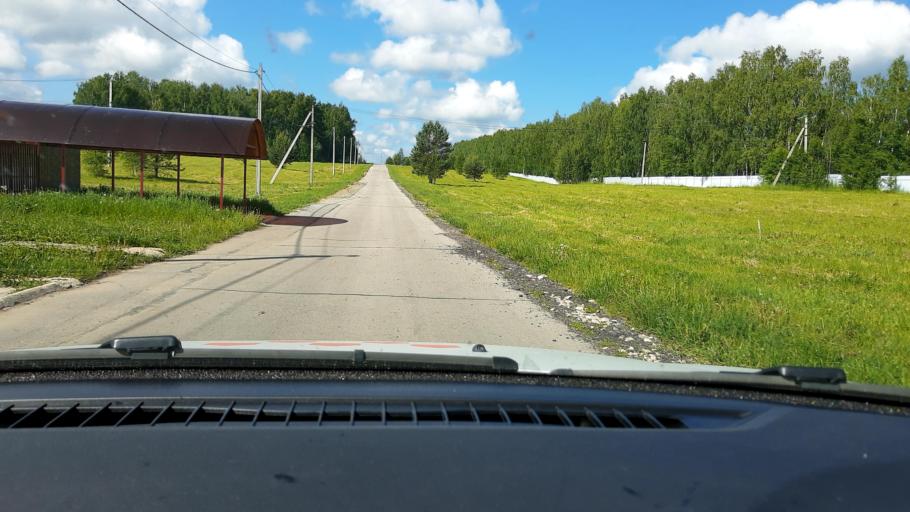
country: RU
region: Nizjnij Novgorod
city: Dal'neye Konstantinovo
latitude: 55.9309
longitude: 43.9971
